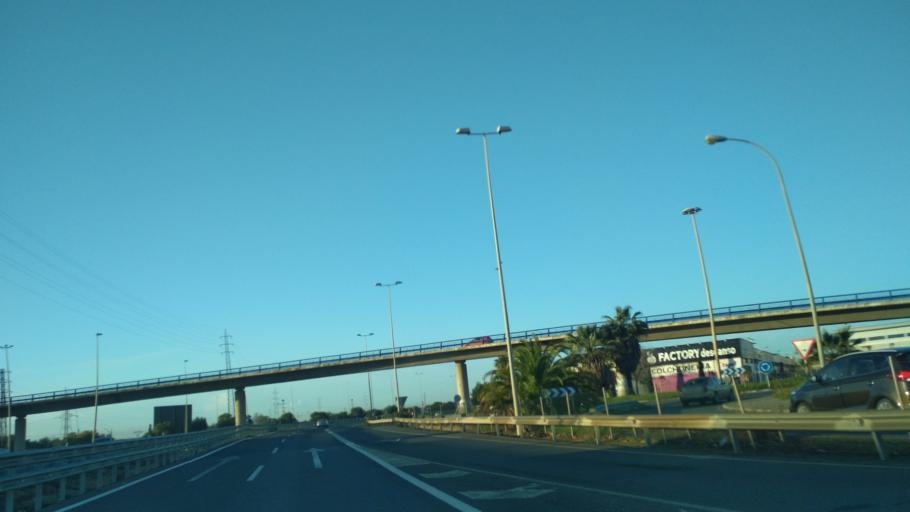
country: ES
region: Andalusia
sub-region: Provincia de Huelva
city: Huelva
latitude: 37.2613
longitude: -6.9201
